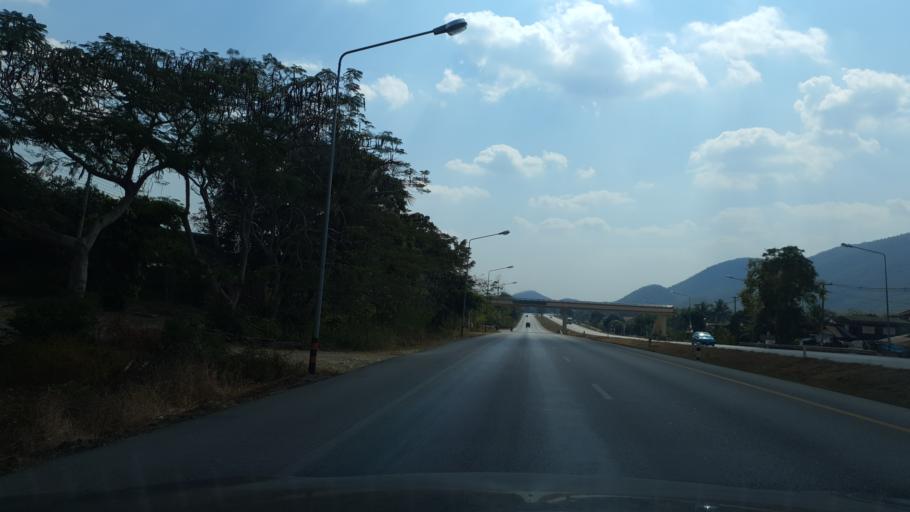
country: TH
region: Lampang
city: Mae Phrik
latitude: 17.3621
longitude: 99.1471
